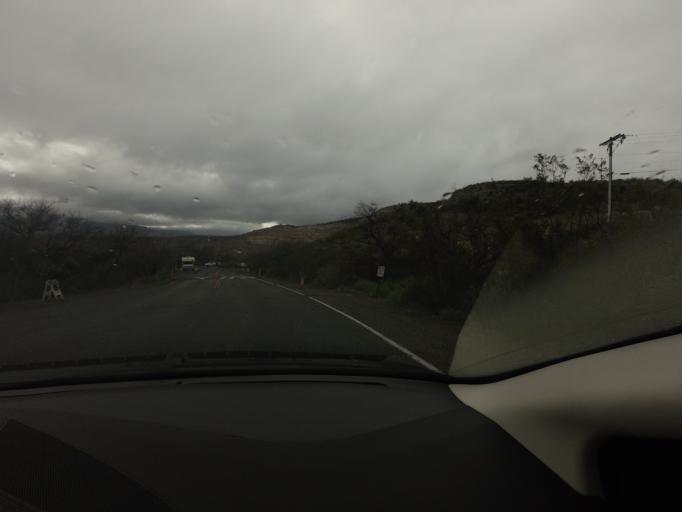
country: US
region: Arizona
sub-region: Yavapai County
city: Camp Verde
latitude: 34.6115
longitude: -111.8376
